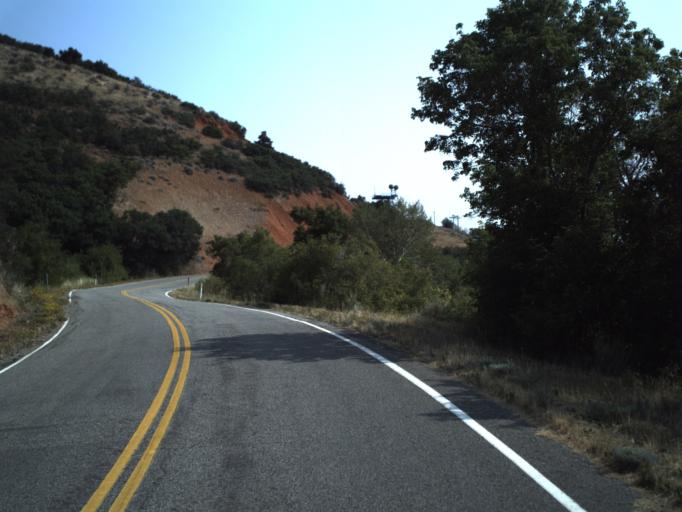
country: US
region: Utah
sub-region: Summit County
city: Summit Park
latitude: 40.8270
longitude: -111.6580
